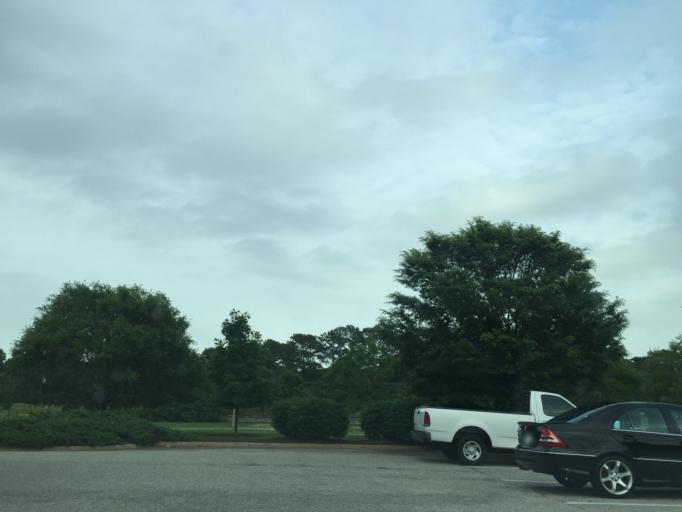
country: US
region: Virginia
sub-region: Isle of Wight County
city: Carrollton
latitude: 37.0906
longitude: -76.5293
